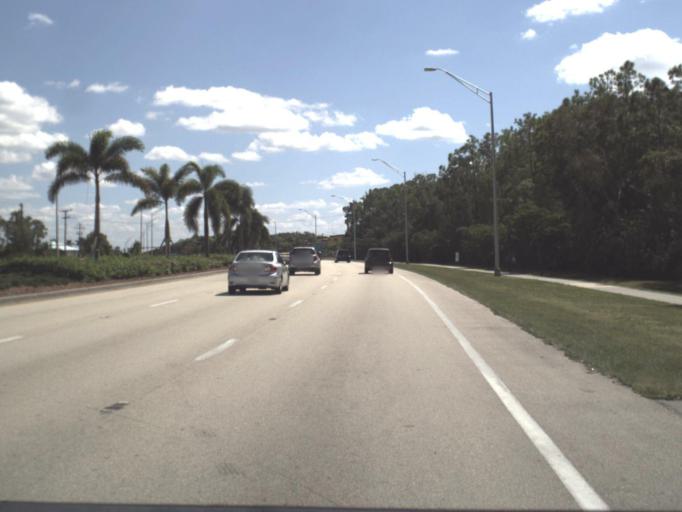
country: US
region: Florida
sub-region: Collier County
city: Naples Manor
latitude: 26.0778
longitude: -81.7214
